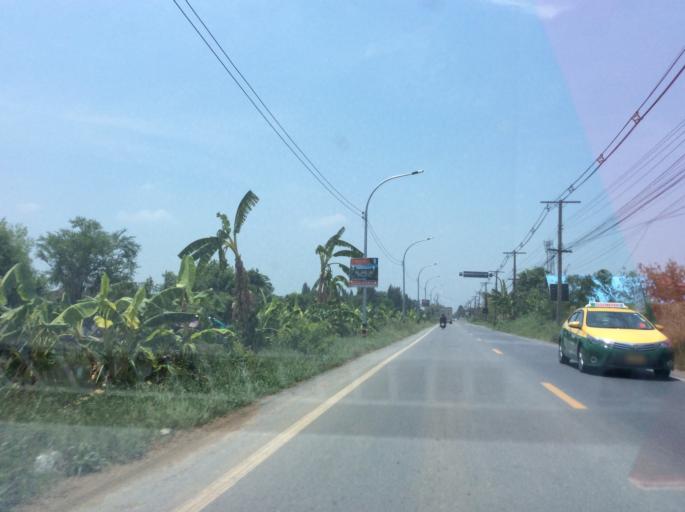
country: TH
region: Pathum Thani
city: Ban Rangsit
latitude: 14.0231
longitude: 100.7785
